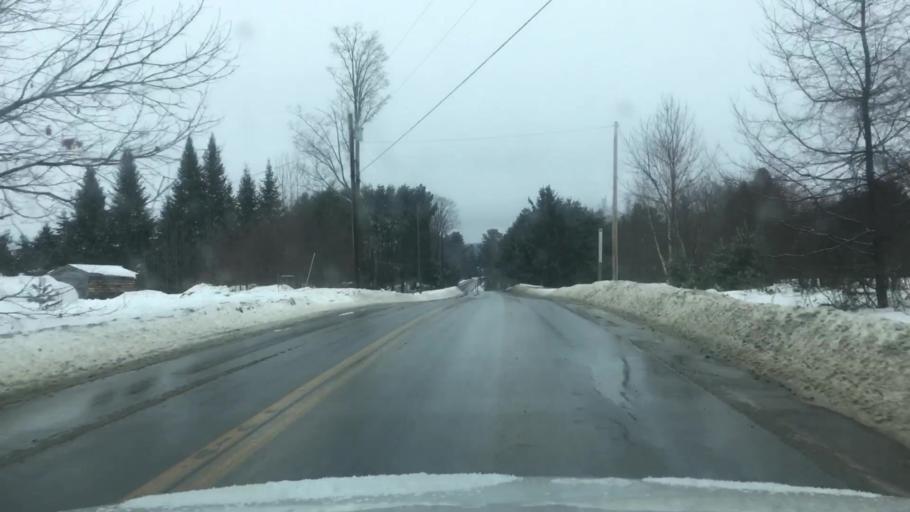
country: US
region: Maine
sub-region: Franklin County
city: Chesterville
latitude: 44.5955
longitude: -70.1348
